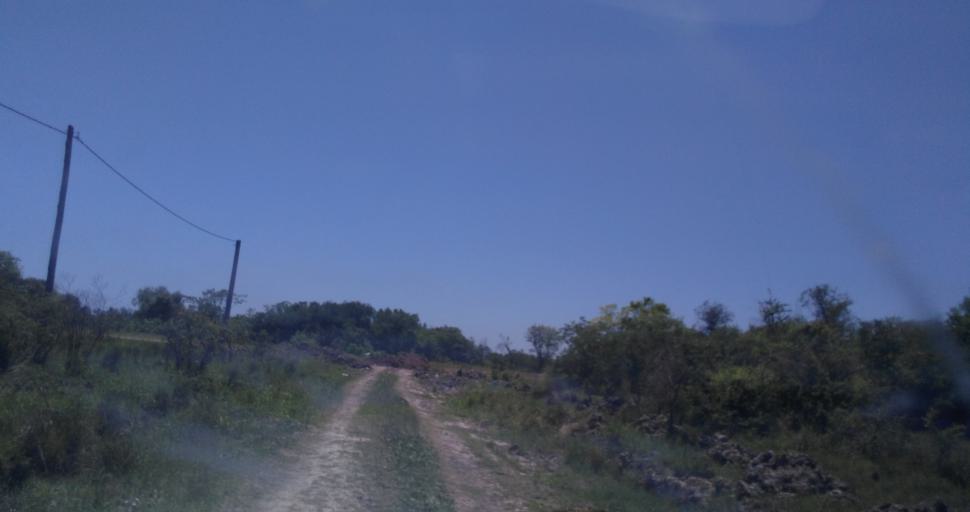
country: AR
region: Chaco
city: Fontana
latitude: -27.4033
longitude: -58.9698
